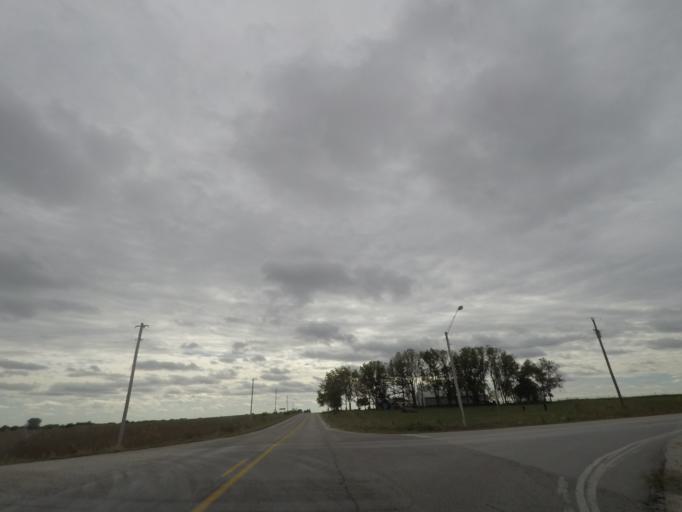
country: US
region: Iowa
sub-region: Story County
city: Nevada
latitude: 41.9141
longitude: -93.4634
